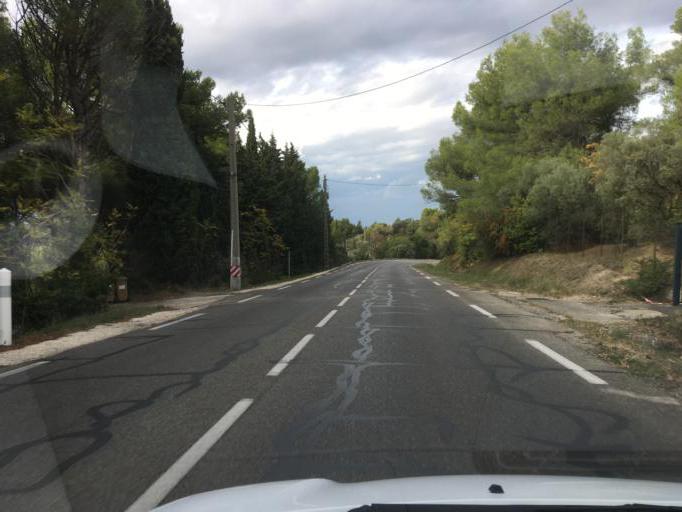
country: FR
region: Provence-Alpes-Cote d'Azur
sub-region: Departement du Vaucluse
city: Jonquerettes
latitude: 43.9324
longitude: 4.9224
